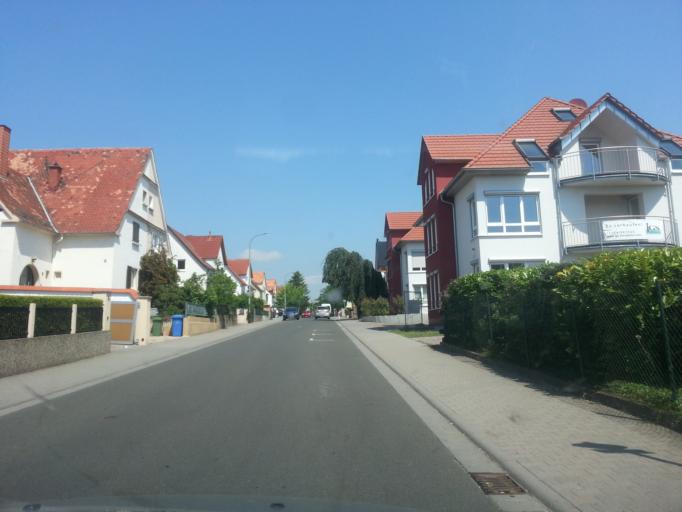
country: DE
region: Rheinland-Pfalz
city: Freinsheim
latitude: 49.5043
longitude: 8.2057
